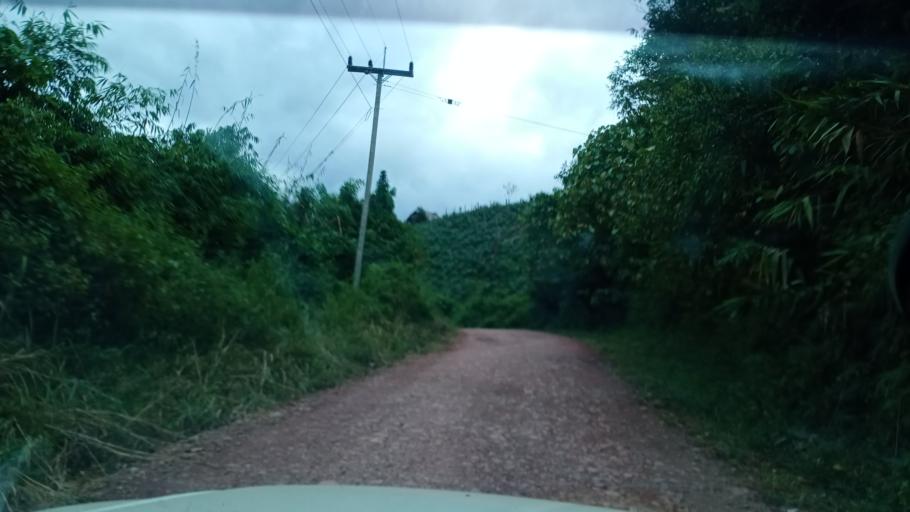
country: TH
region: Changwat Bueng Kan
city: Pak Khat
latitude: 18.7203
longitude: 103.2300
